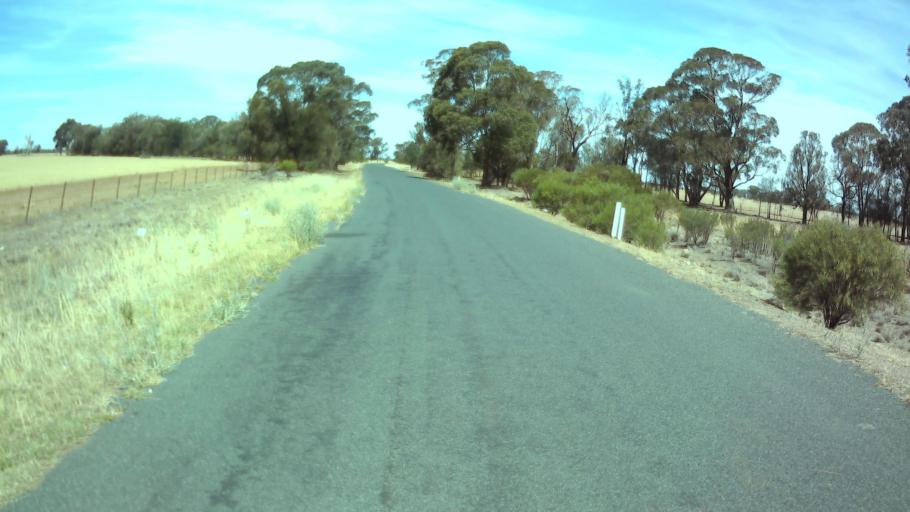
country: AU
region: New South Wales
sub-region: Weddin
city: Grenfell
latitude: -33.9568
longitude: 147.7780
